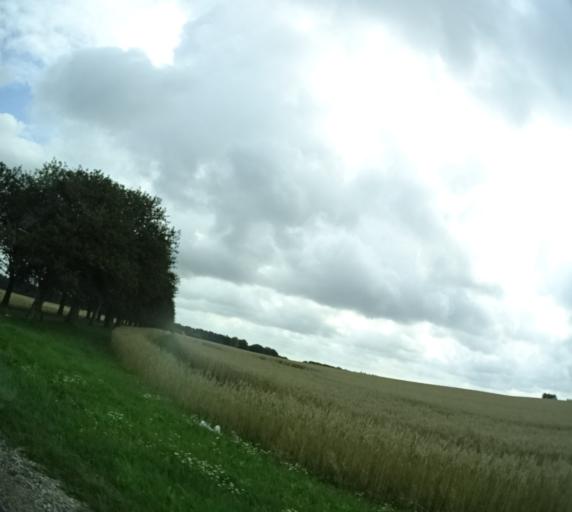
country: DK
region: Central Jutland
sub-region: Syddjurs Kommune
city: Ryomgard
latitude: 56.3908
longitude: 10.5110
